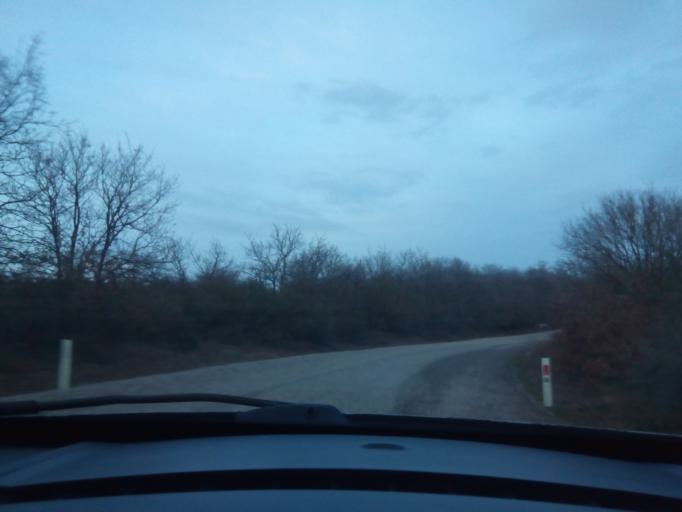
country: TR
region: Balikesir
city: Omerkoy
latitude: 39.9048
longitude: 28.0318
